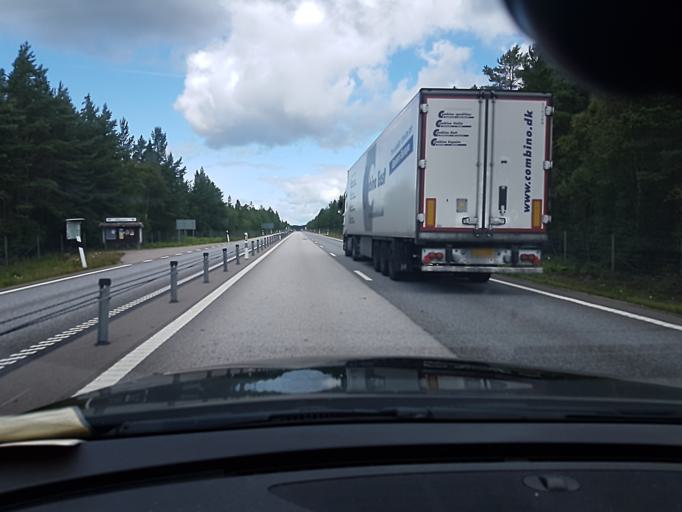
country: SE
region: Kronoberg
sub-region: Lessebo Kommun
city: Hovmantorp
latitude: 56.7983
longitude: 15.1167
